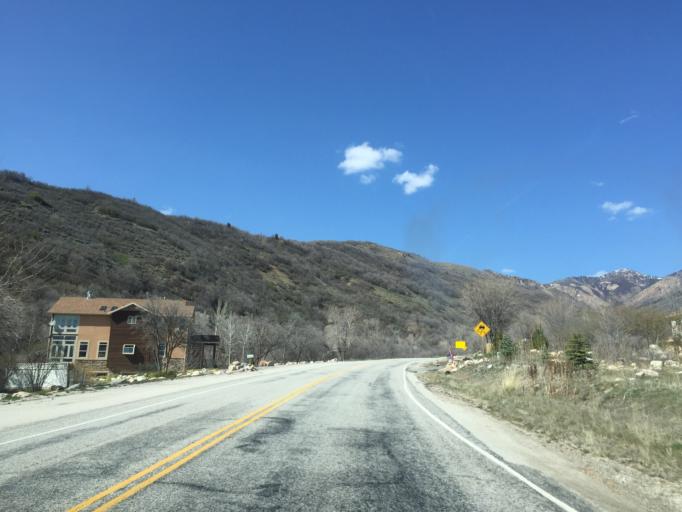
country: US
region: Utah
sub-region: Weber County
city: Wolf Creek
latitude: 41.3398
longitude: -111.8256
